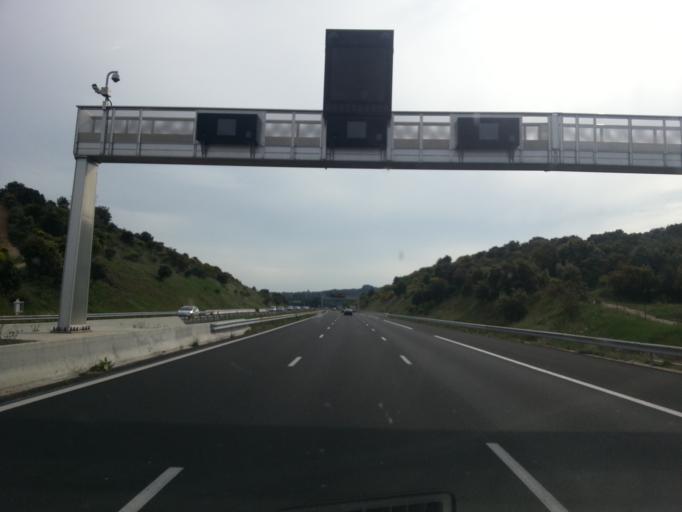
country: FR
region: Languedoc-Roussillon
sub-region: Departement du Gard
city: Tavel
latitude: 44.0144
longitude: 4.7195
